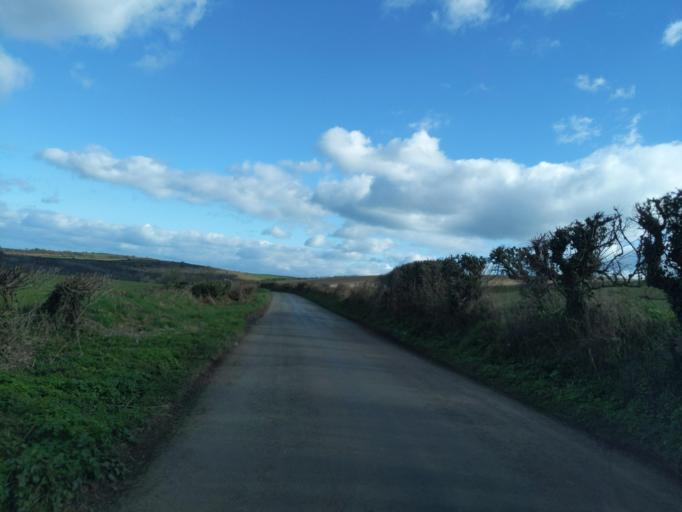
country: GB
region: England
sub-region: Devon
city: Salcombe
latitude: 50.2578
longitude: -3.7111
